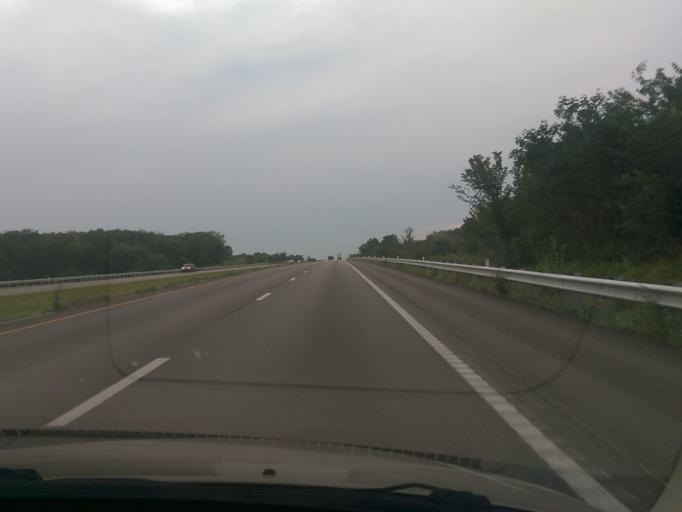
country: US
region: Missouri
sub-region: Andrew County
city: Savannah
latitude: 39.9453
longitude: -94.9427
